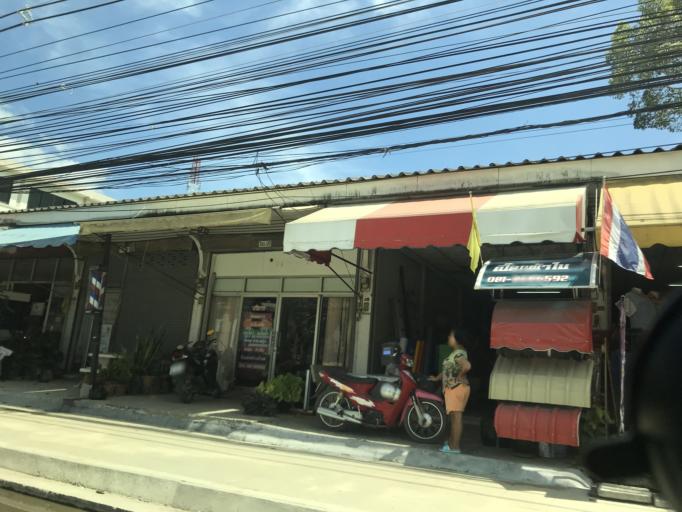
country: TH
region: Surat Thani
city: Ko Samui
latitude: 9.5527
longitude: 100.0339
